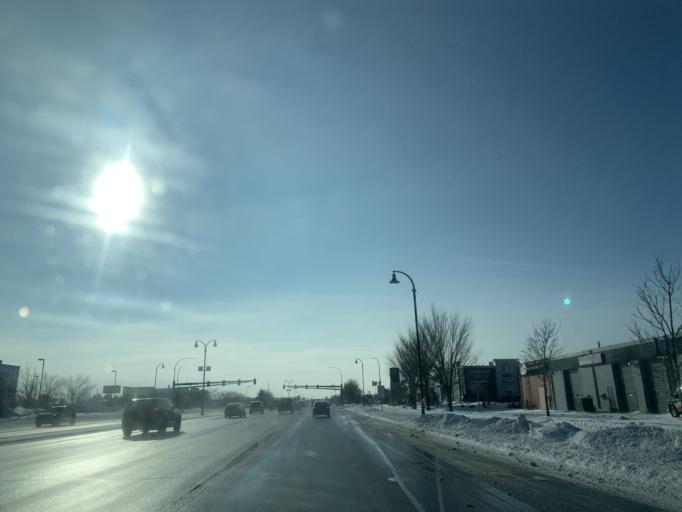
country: US
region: Minnesota
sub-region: Dakota County
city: Apple Valley
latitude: 44.7366
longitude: -93.2179
